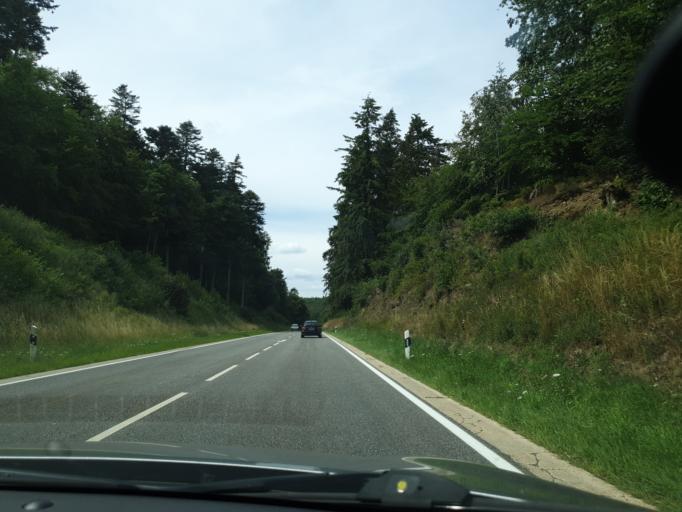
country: DE
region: Rheinland-Pfalz
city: Reudelsterz
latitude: 50.3295
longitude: 7.1753
